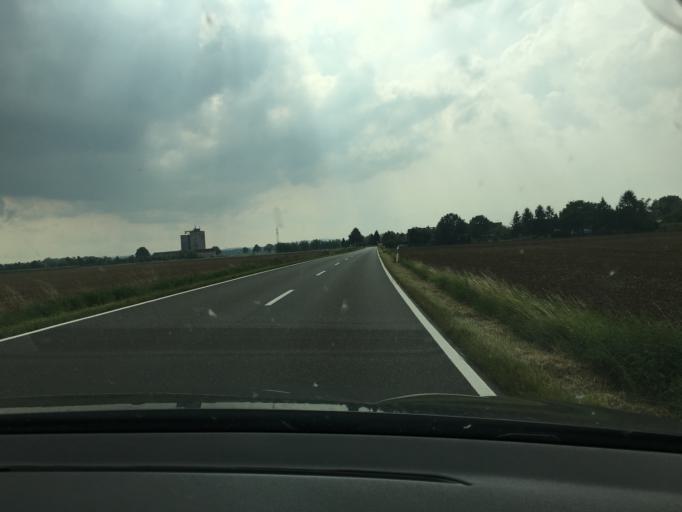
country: DE
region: North Rhine-Westphalia
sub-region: Regierungsbezirk Koln
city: Merzenich
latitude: 50.7833
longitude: 6.5572
